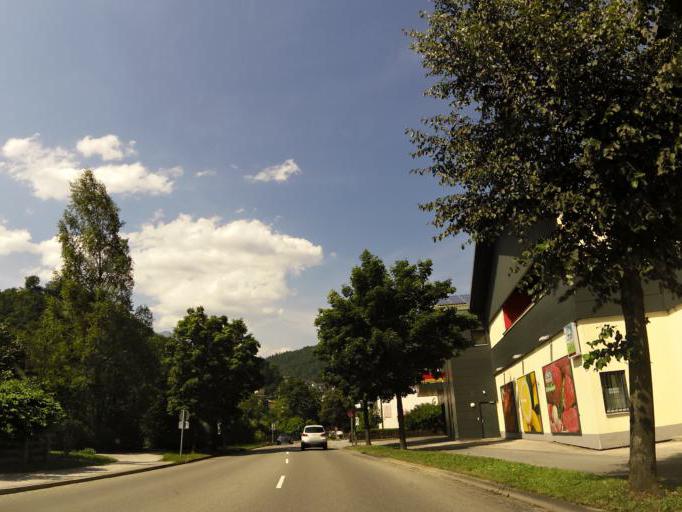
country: DE
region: Bavaria
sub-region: Upper Bavaria
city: Berchtesgaden
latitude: 47.6318
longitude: 13.0071
